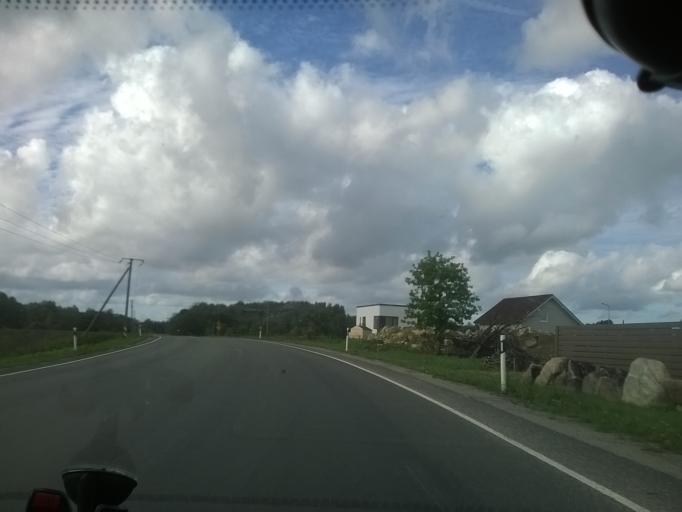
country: EE
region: Harju
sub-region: Rae vald
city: Jueri
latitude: 59.3664
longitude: 24.9235
